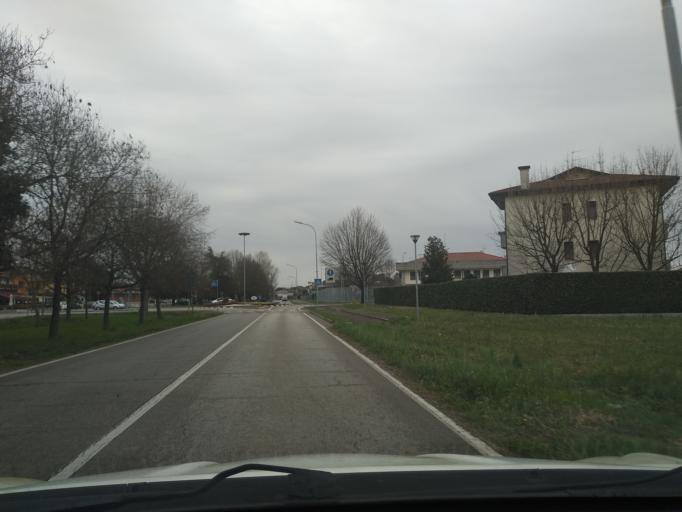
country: IT
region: Veneto
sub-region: Provincia di Padova
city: Selvazzano Dentro
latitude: 45.3895
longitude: 11.7884
